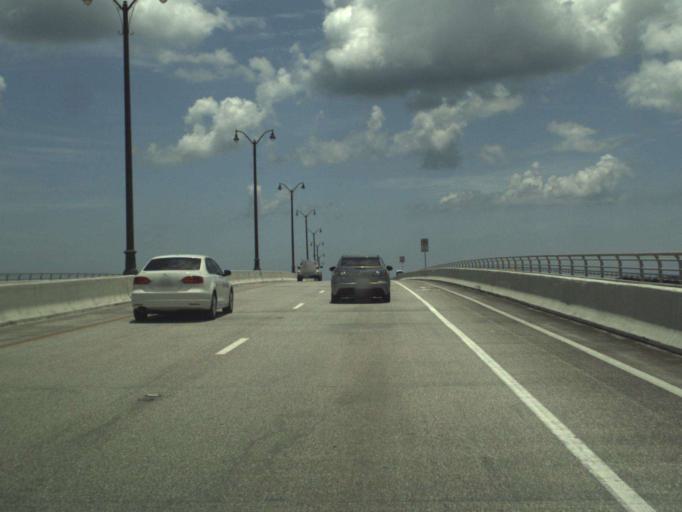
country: US
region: Florida
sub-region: Martin County
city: Sewall's Point
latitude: 27.1985
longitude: -80.2086
